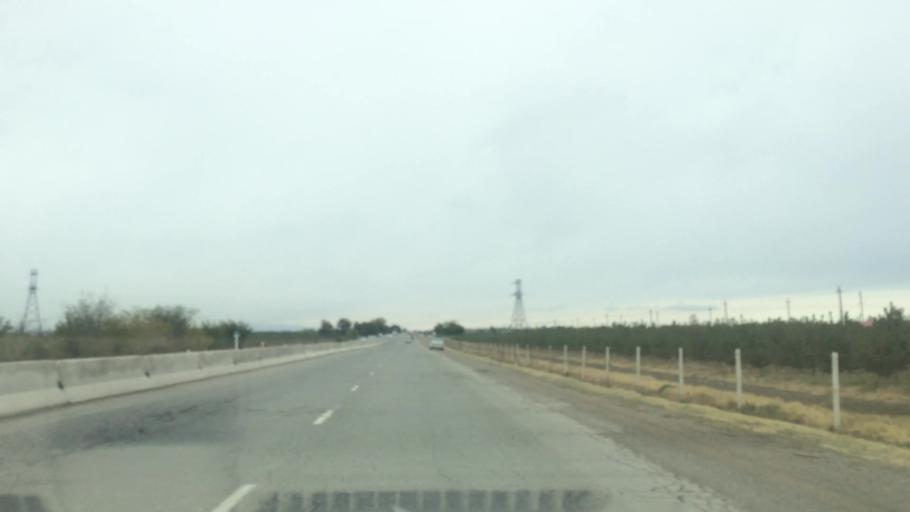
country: UZ
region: Samarqand
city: Bulung'ur
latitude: 39.7562
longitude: 67.2410
